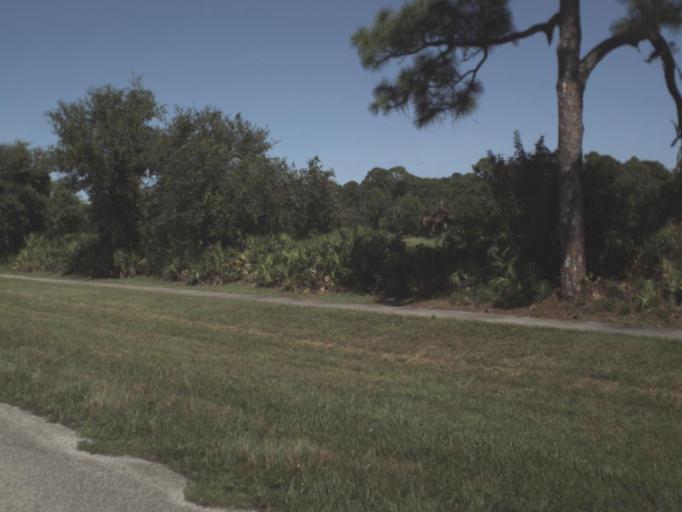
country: US
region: Florida
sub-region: Lee County
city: San Carlos Park
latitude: 26.4704
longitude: -81.8348
